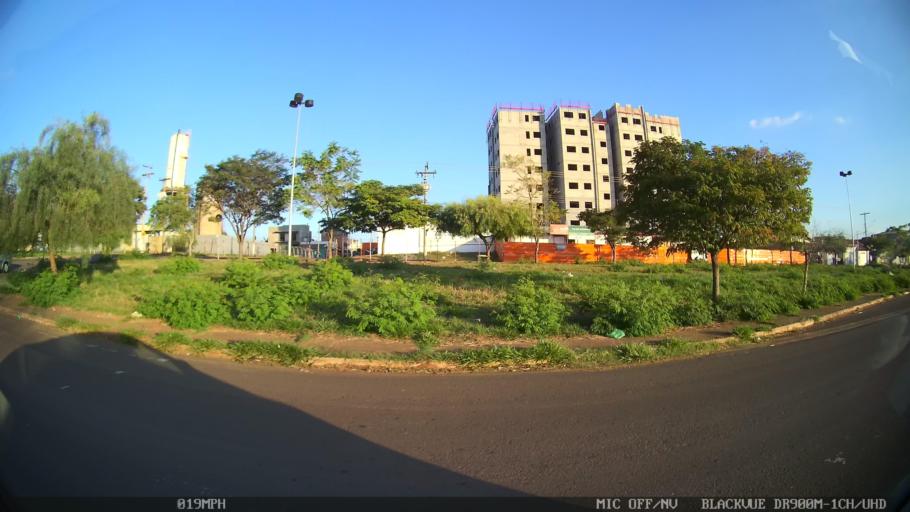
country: BR
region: Sao Paulo
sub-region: Santa Barbara D'Oeste
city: Santa Barbara d'Oeste
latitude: -22.7331
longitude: -47.3836
